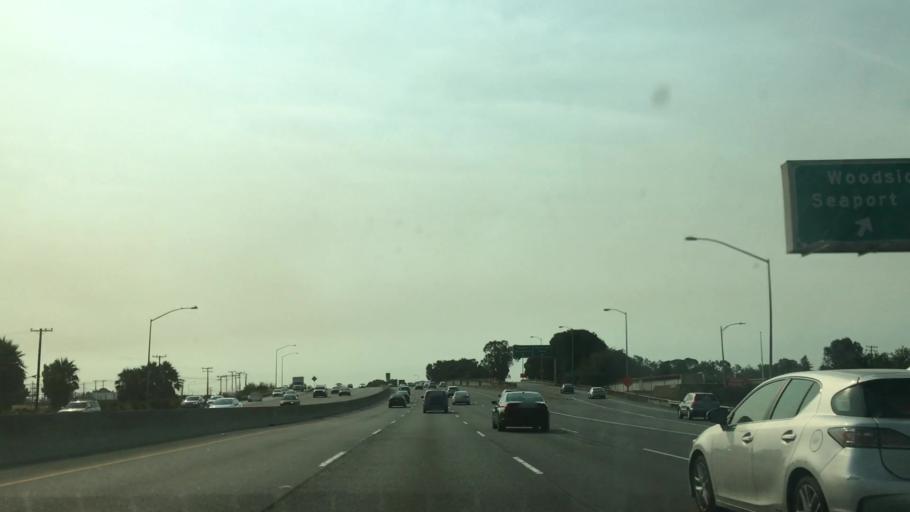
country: US
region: California
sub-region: San Mateo County
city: Redwood City
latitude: 37.4913
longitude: -122.2175
